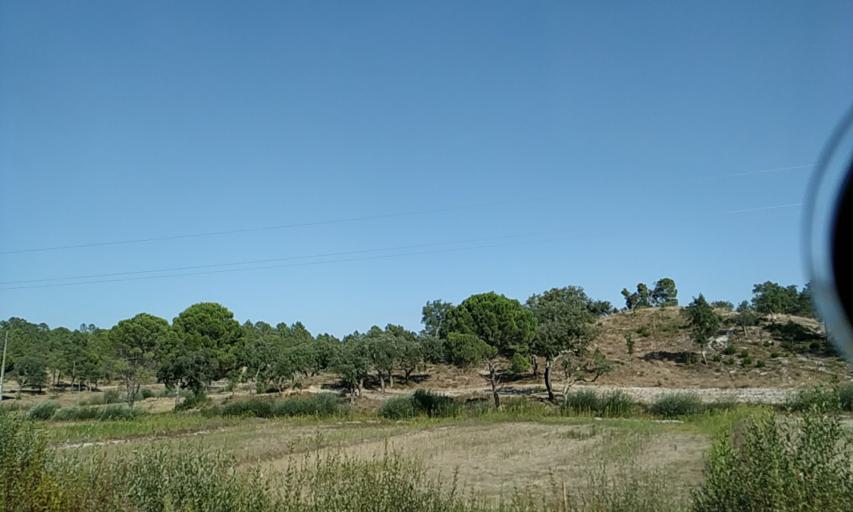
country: PT
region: Evora
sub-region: Vendas Novas
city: Vendas Novas
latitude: 38.7932
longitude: -8.5793
